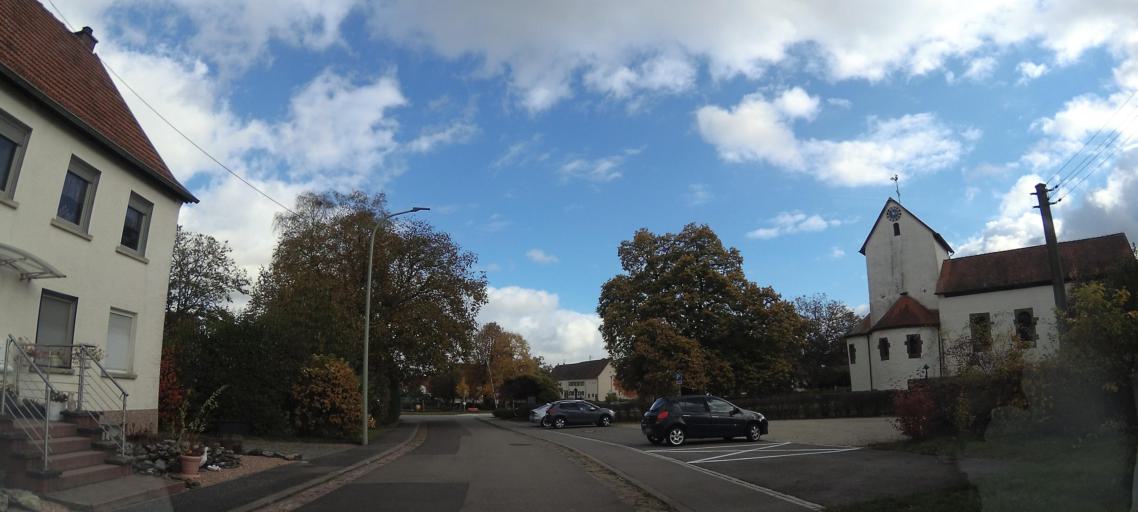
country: DE
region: Saarland
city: Blieskastel
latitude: 49.1822
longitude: 7.2915
